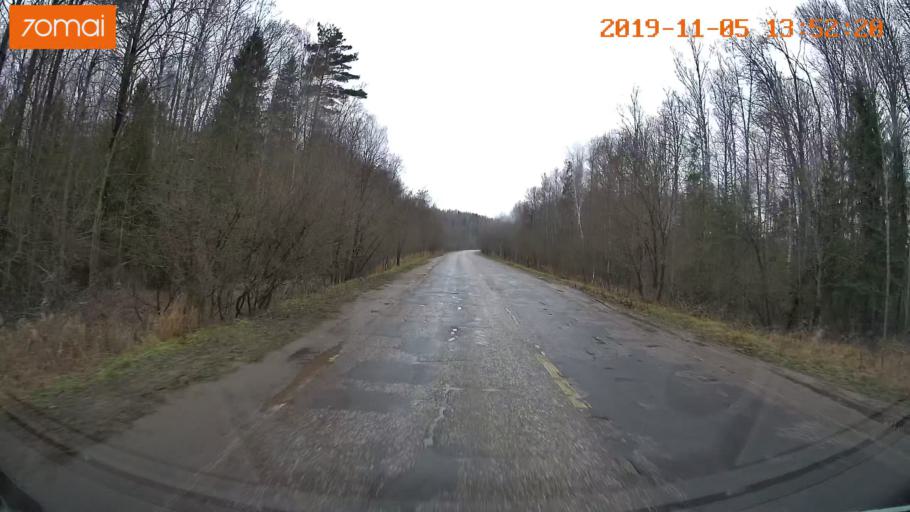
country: RU
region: Ivanovo
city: Kaminskiy
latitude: 57.0273
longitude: 41.3877
